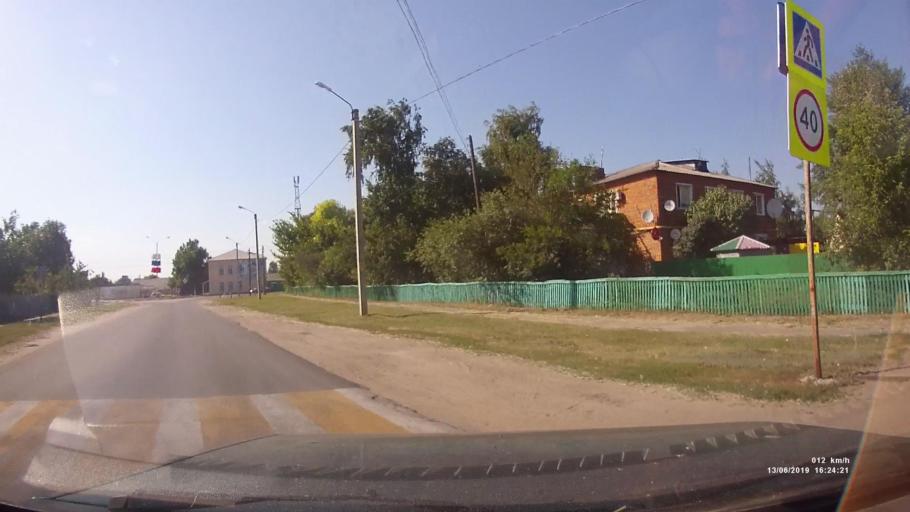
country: RU
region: Rostov
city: Kazanskaya
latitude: 49.7976
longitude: 41.1459
